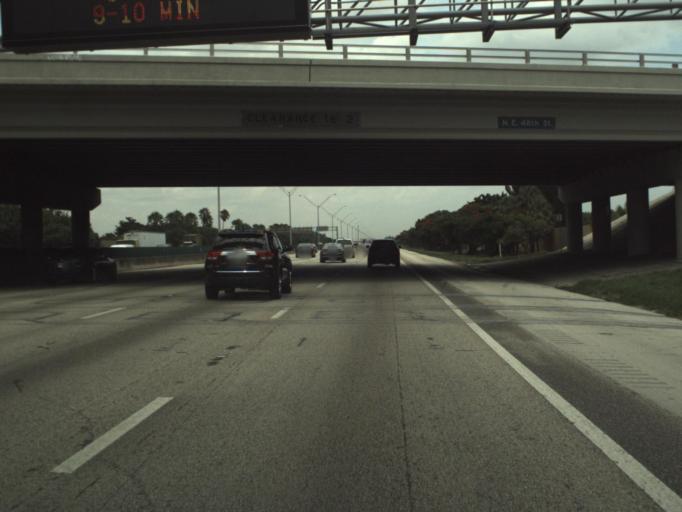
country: US
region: Florida
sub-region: Broward County
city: Tedder
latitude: 26.2893
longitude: -80.1238
